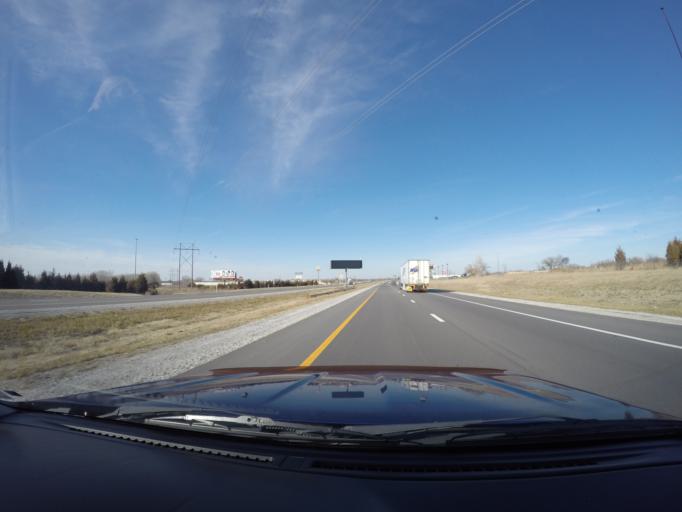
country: US
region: Kansas
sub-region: Sedgwick County
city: Park City
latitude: 37.7893
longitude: -97.3268
